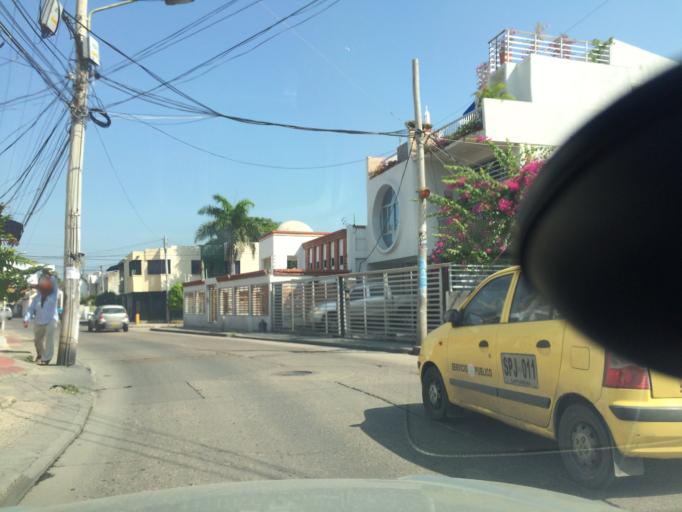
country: CO
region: Bolivar
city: Cartagena
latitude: 10.4165
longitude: -75.5362
